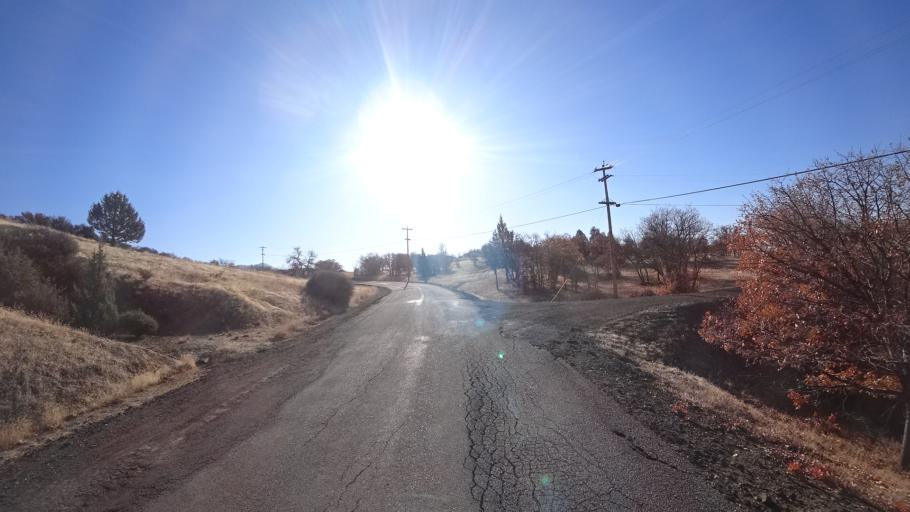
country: US
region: California
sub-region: Siskiyou County
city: Montague
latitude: 41.8777
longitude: -122.4712
